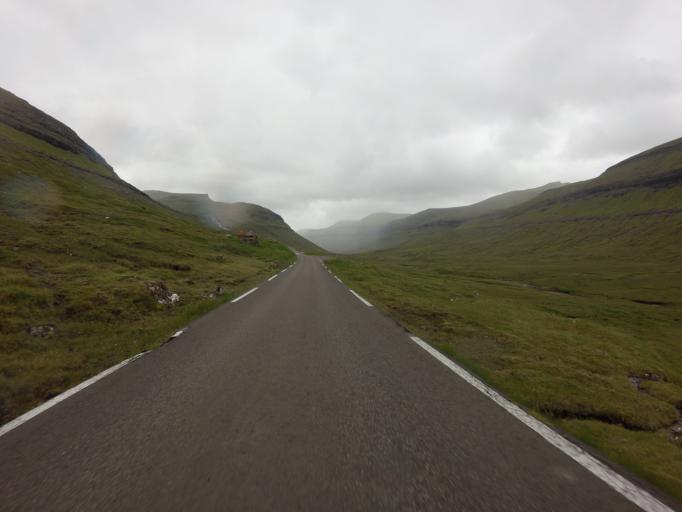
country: FO
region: Streymoy
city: Vestmanna
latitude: 62.2158
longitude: -7.1181
